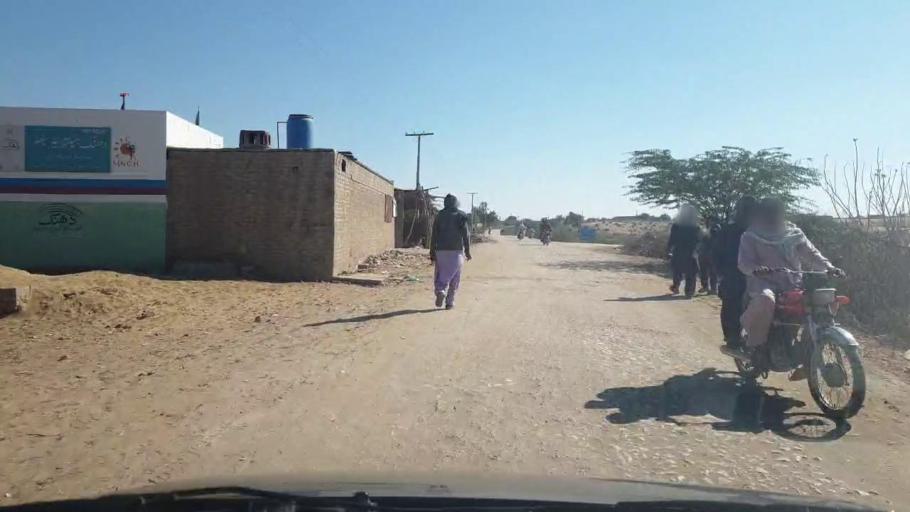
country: PK
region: Sindh
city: Bozdar
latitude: 27.0637
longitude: 68.6237
